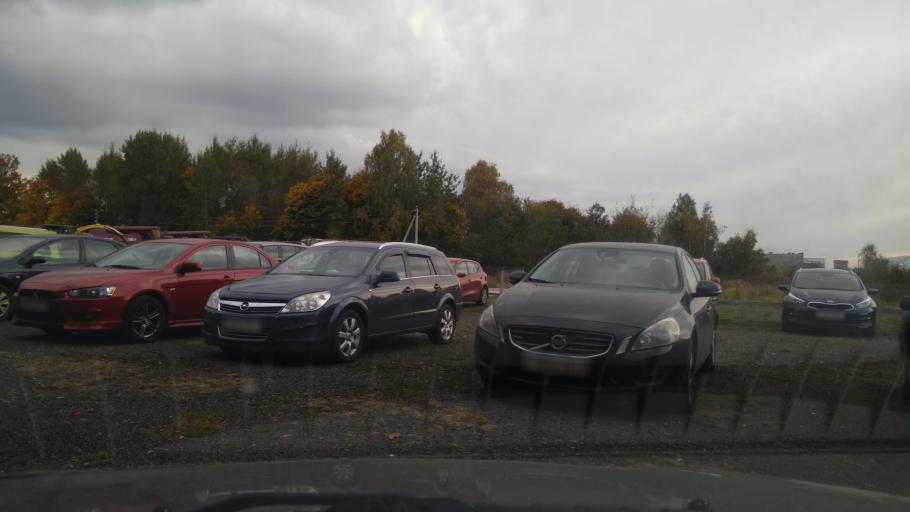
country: BY
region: Minsk
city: Dukora
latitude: 53.6770
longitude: 27.9626
